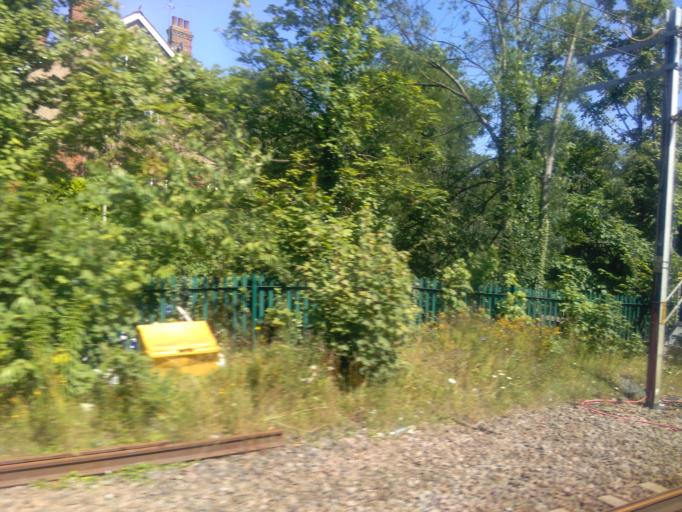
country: GB
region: England
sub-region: Hertfordshire
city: Harpenden
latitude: 51.8160
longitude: -0.3523
